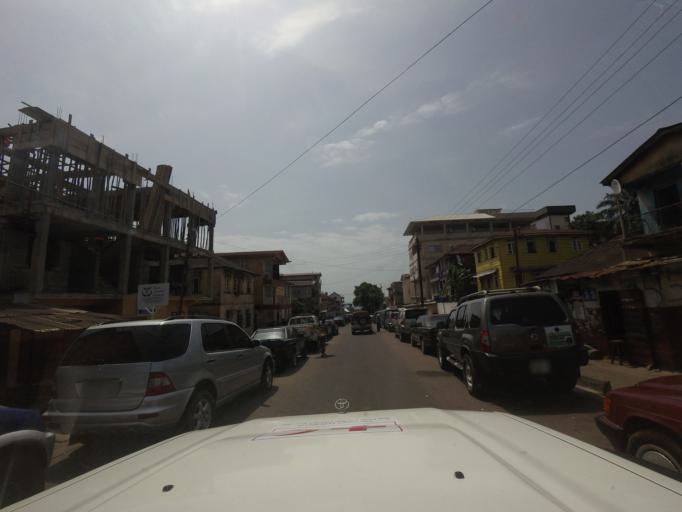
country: SL
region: Western Area
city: Freetown
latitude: 8.4847
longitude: -13.2363
